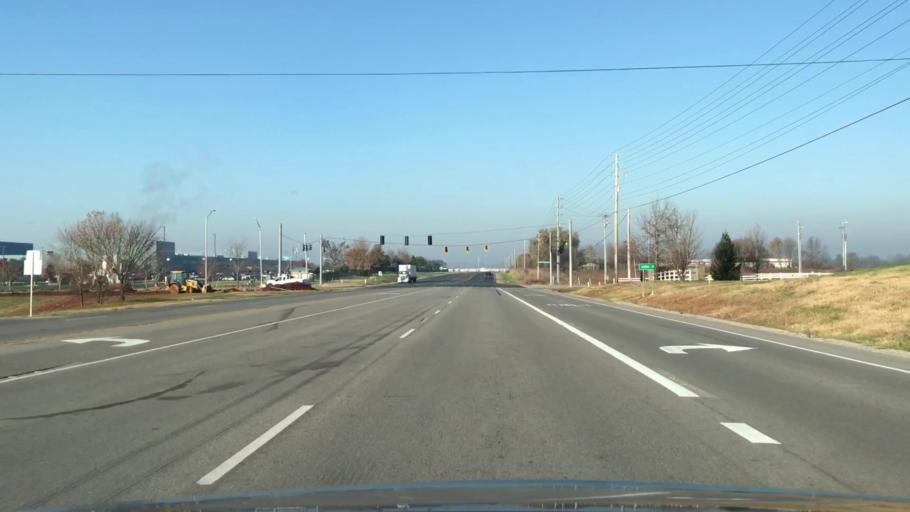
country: US
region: Kentucky
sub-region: Warren County
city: Bowling Green
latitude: 37.0331
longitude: -86.3169
